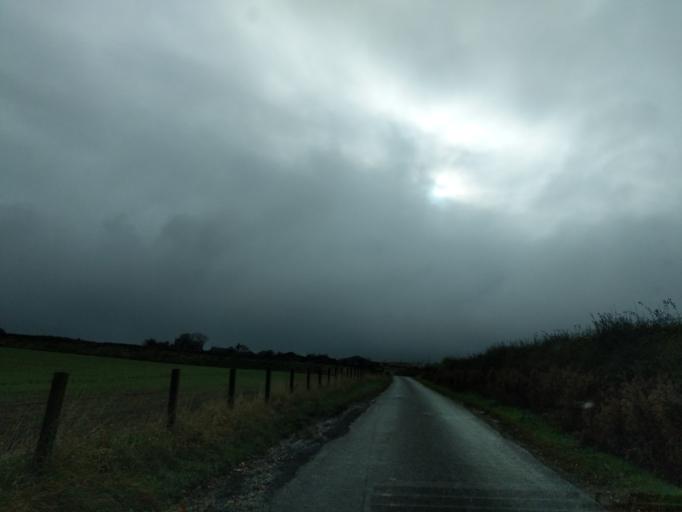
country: GB
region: Scotland
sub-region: East Lothian
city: Dunbar
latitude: 55.9529
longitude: -2.3974
